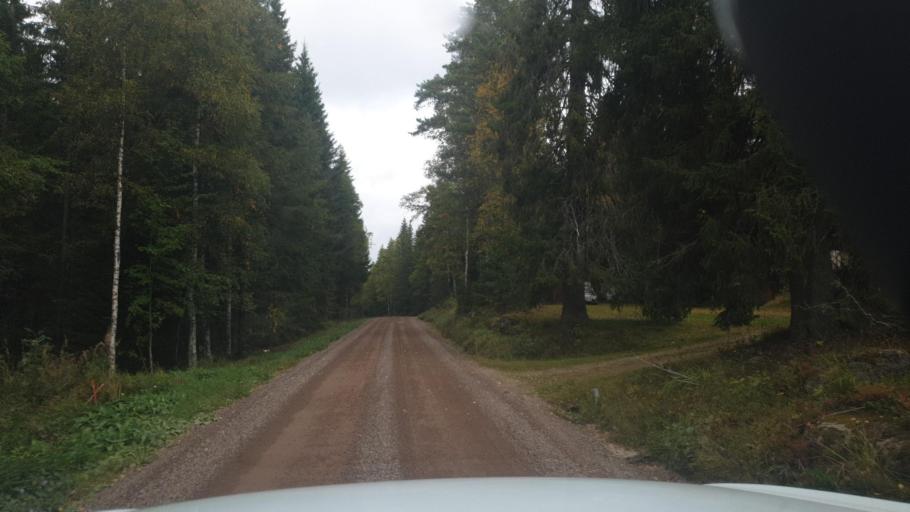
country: SE
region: Vaermland
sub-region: Arvika Kommun
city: Arvika
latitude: 59.9770
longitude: 12.6609
